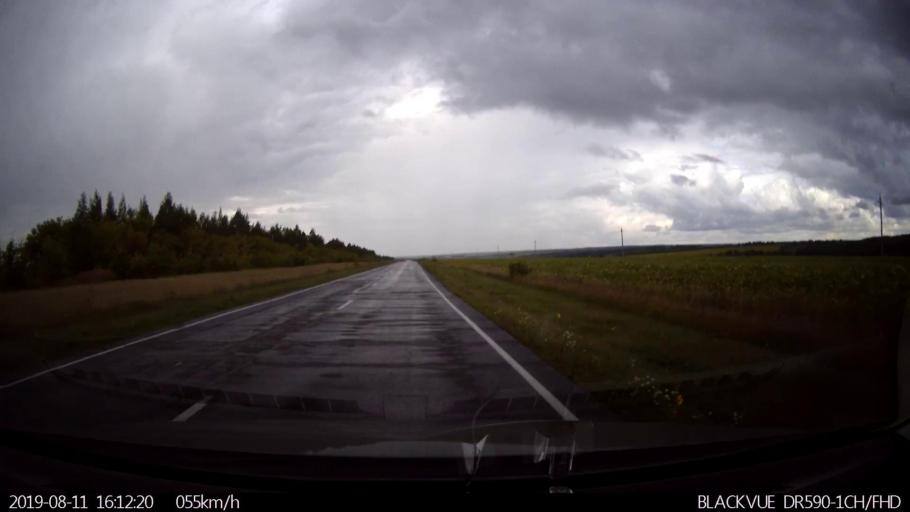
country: RU
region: Ulyanovsk
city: Ignatovka
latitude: 54.0106
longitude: 47.6408
